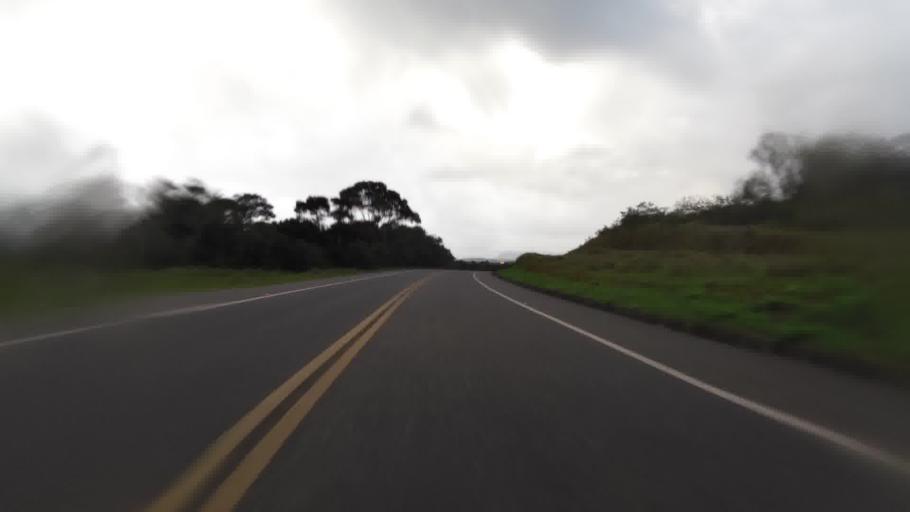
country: BR
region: Espirito Santo
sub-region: Guarapari
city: Guarapari
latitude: -20.7179
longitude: -40.5758
